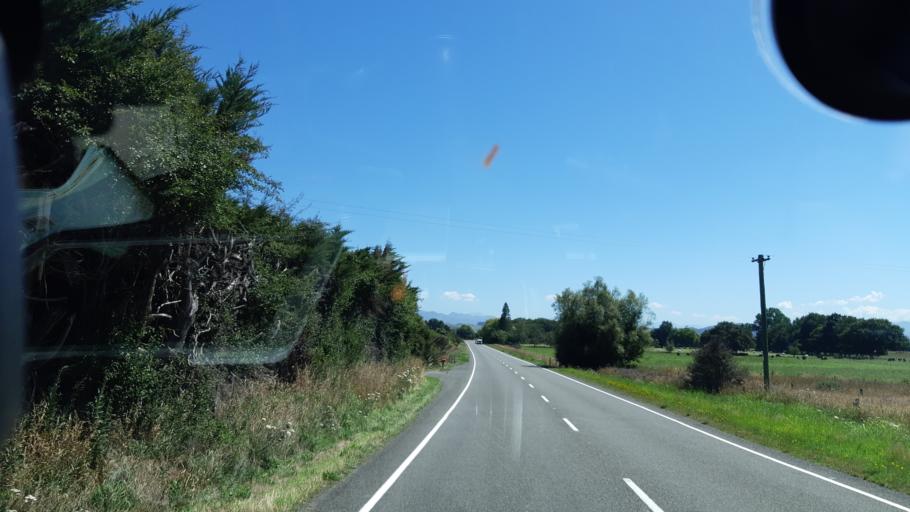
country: NZ
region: Canterbury
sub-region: Kaikoura District
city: Kaikoura
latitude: -42.7457
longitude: 173.2671
